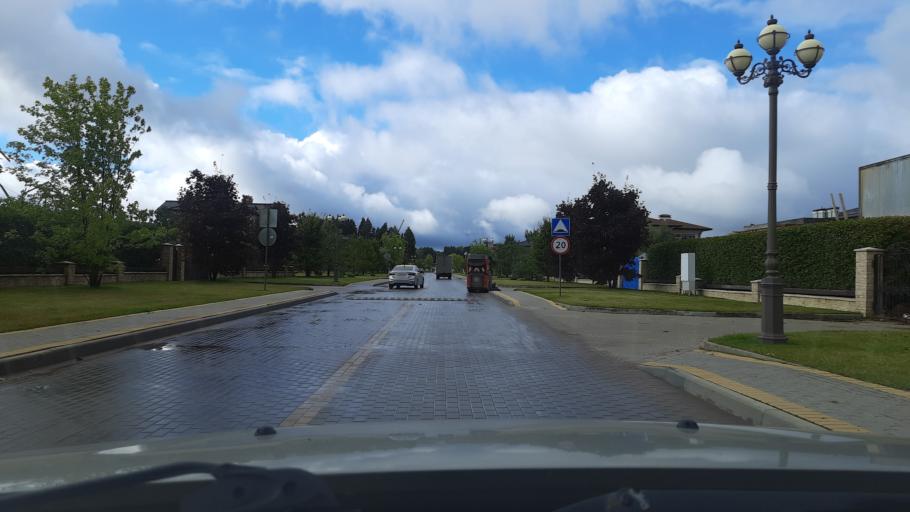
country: RU
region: Moskovskaya
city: Nikolina Gora
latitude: 55.7708
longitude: 37.0423
